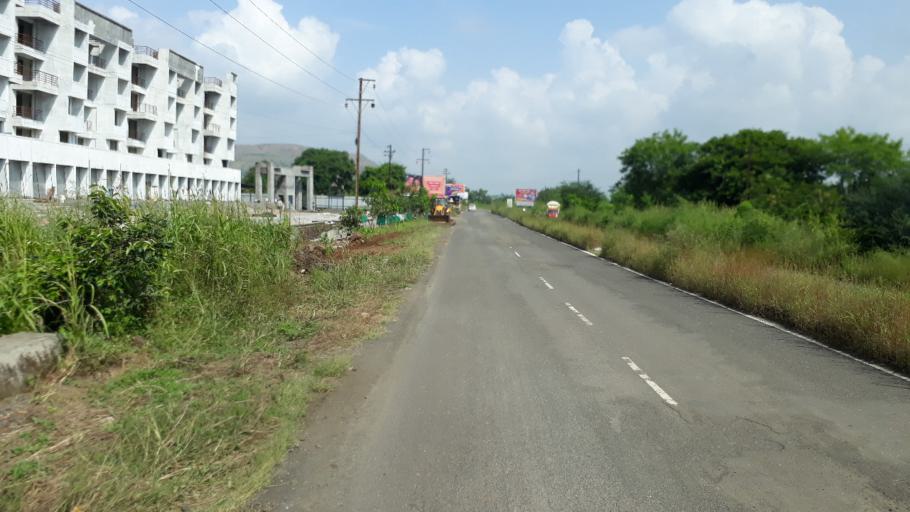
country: IN
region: Maharashtra
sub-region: Raigarh
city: Neral
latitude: 18.9870
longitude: 73.3277
